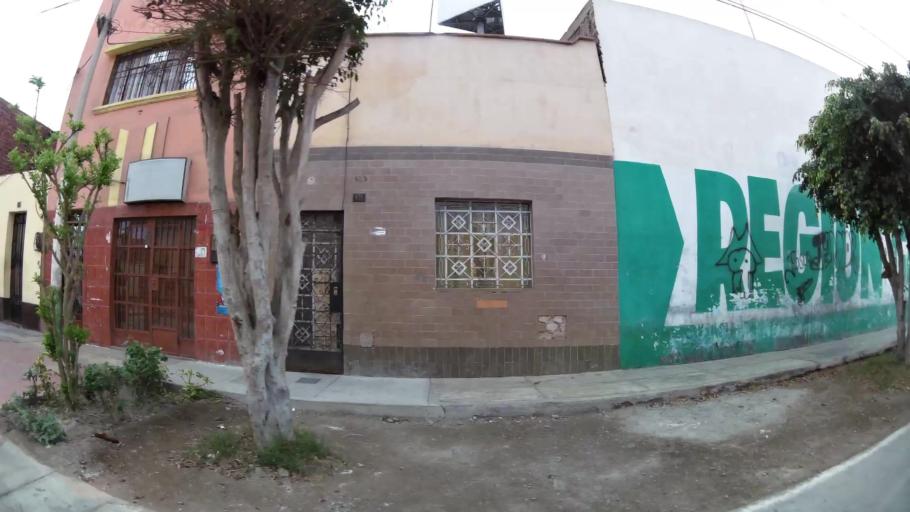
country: PE
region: Callao
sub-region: Callao
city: Callao
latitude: -12.0558
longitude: -77.1342
